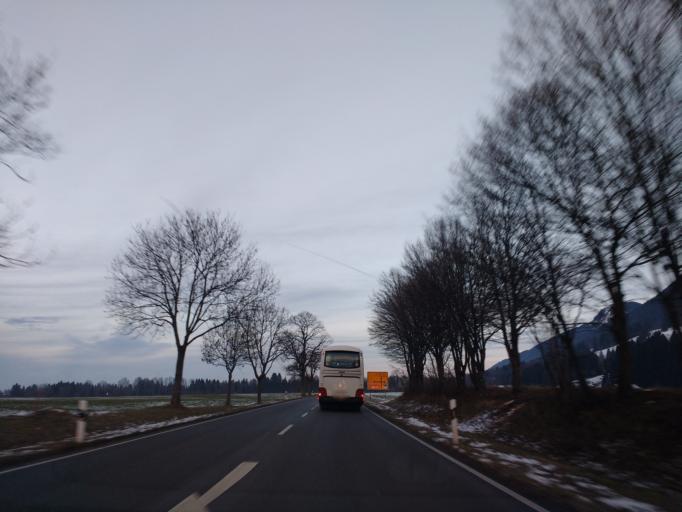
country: DE
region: Bavaria
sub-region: Swabia
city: Halblech
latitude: 47.6221
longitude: 10.8112
